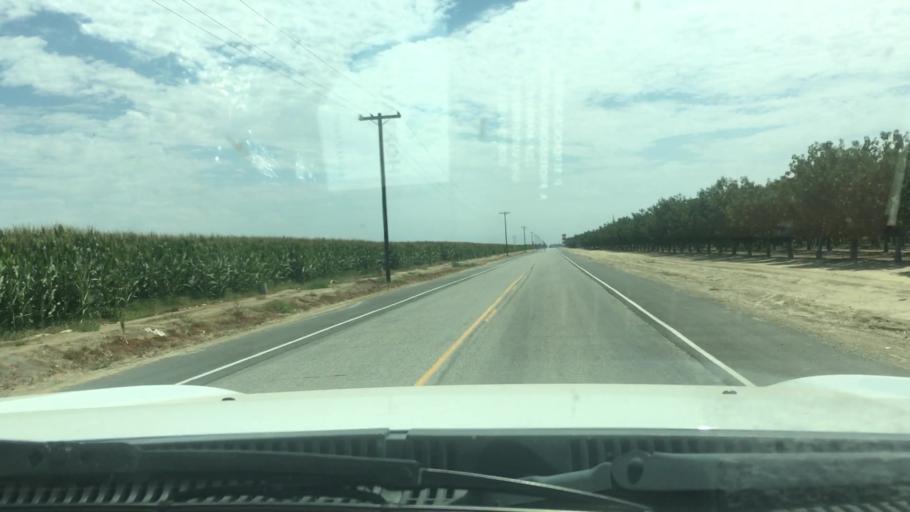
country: US
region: California
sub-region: Kern County
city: Wasco
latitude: 35.5579
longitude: -119.4201
